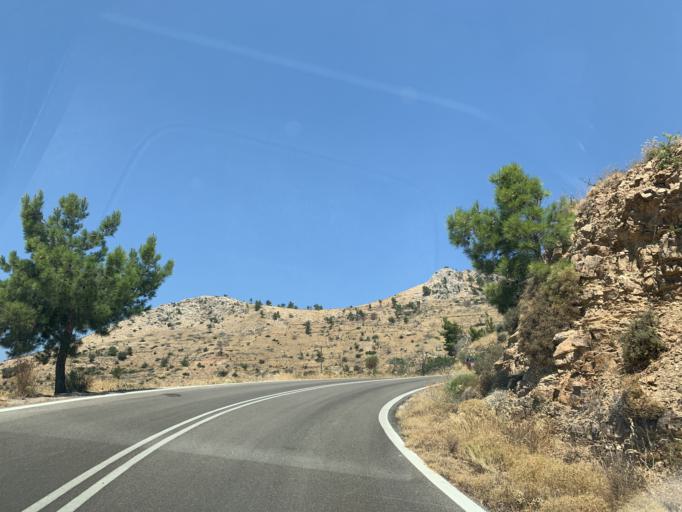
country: GR
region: North Aegean
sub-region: Chios
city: Vrontados
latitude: 38.4520
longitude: 25.9775
